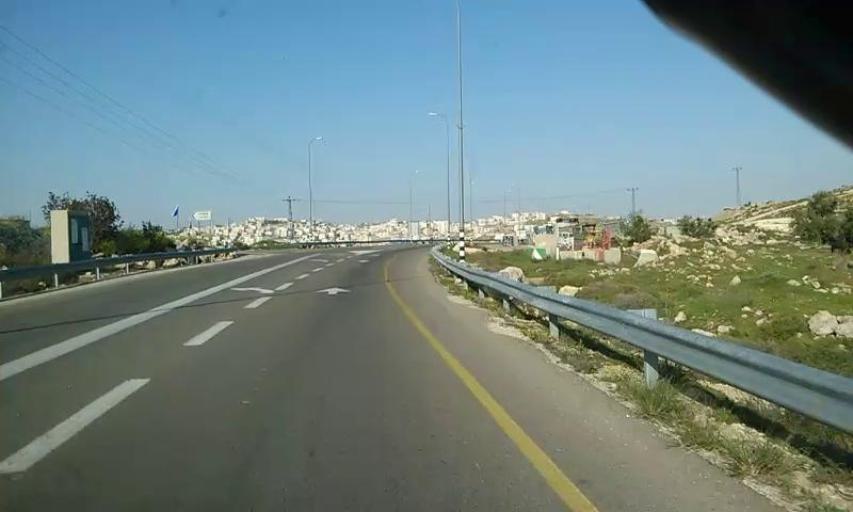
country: PS
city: Khallat ad Dar
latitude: 31.5024
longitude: 35.1076
